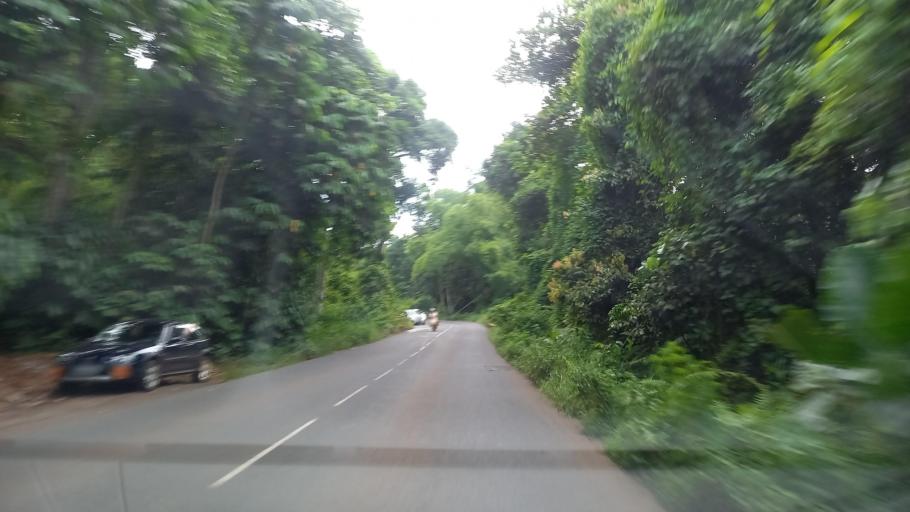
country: YT
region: Bandraboua
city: Bandraboua
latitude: -12.7337
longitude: 45.1190
